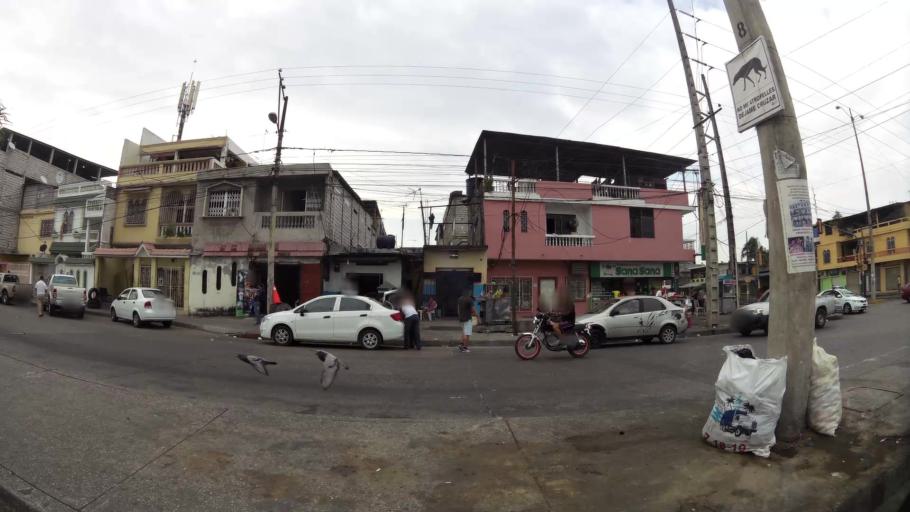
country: EC
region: Guayas
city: Guayaquil
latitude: -2.2511
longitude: -79.8903
